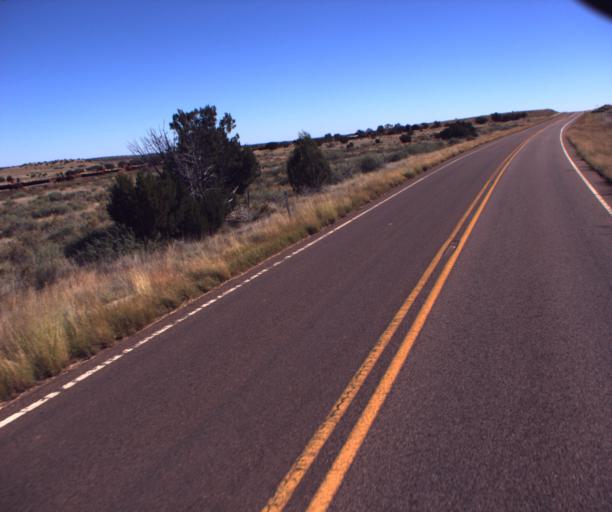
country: US
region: Arizona
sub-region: Navajo County
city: Snowflake
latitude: 34.5127
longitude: -110.1541
